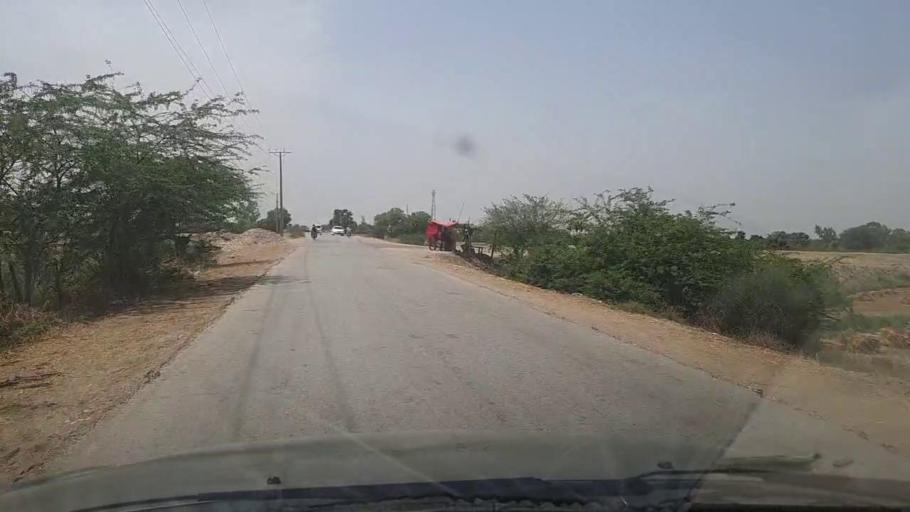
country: PK
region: Sindh
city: Bhiria
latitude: 26.9049
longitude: 68.2023
